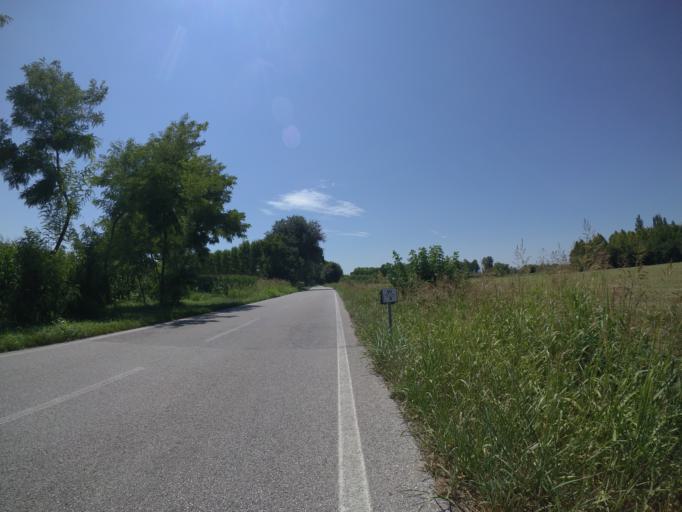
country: IT
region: Friuli Venezia Giulia
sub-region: Provincia di Udine
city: Talmassons
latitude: 45.9166
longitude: 13.1395
